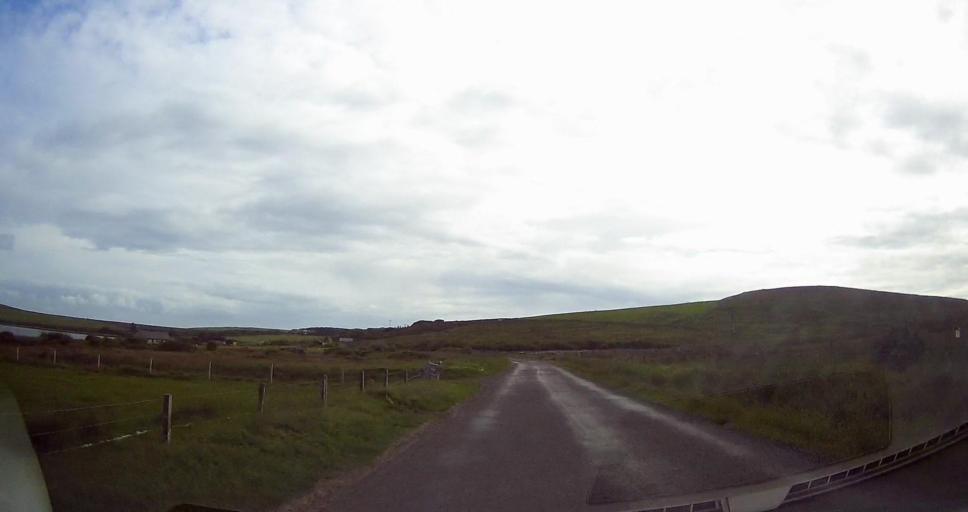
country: GB
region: Scotland
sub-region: Orkney Islands
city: Stromness
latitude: 58.7925
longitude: -3.2569
